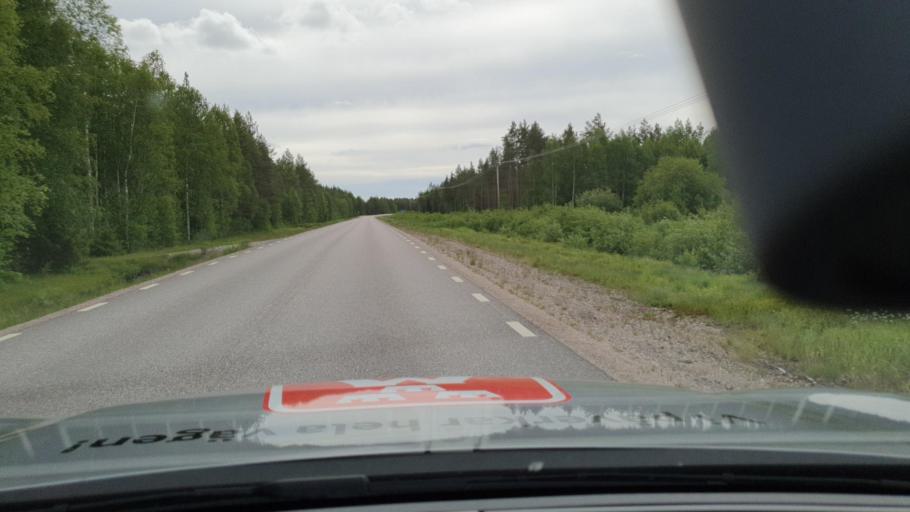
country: SE
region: Norrbotten
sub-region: Kalix Kommun
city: Kalix
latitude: 65.8797
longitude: 23.4816
